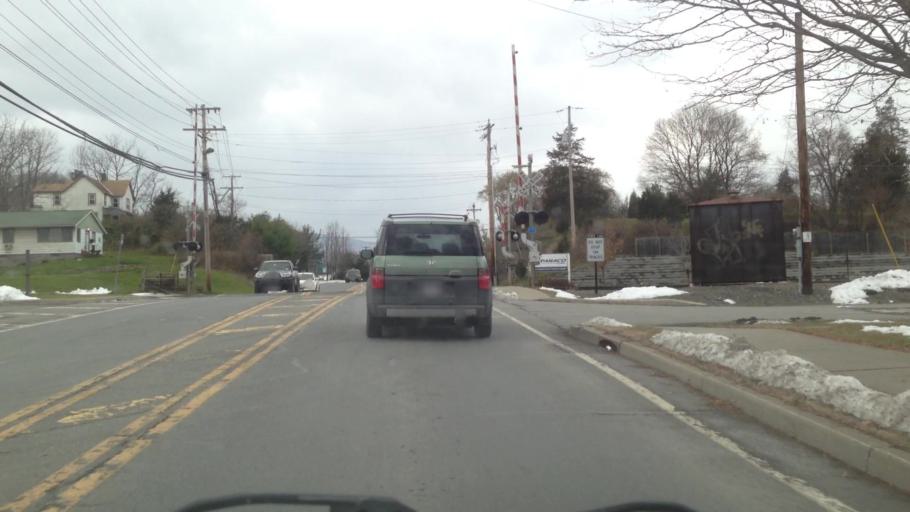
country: US
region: New York
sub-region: Ulster County
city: Saugerties
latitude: 42.0823
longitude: -73.9653
